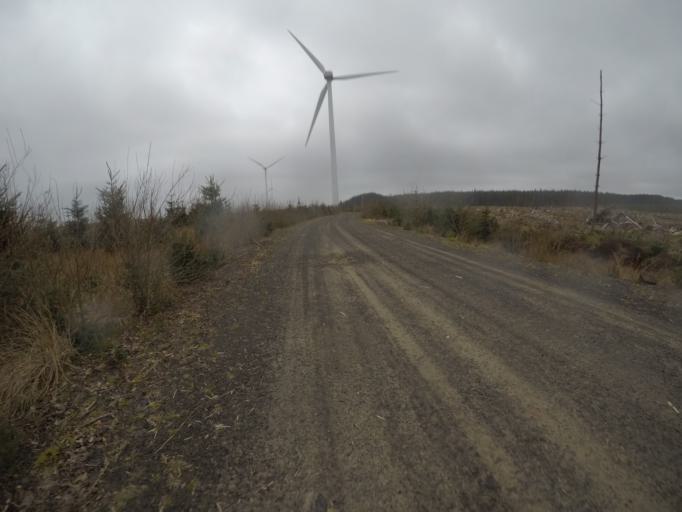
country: GB
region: Scotland
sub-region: East Ayrshire
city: Newmilns
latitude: 55.6451
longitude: -4.3237
